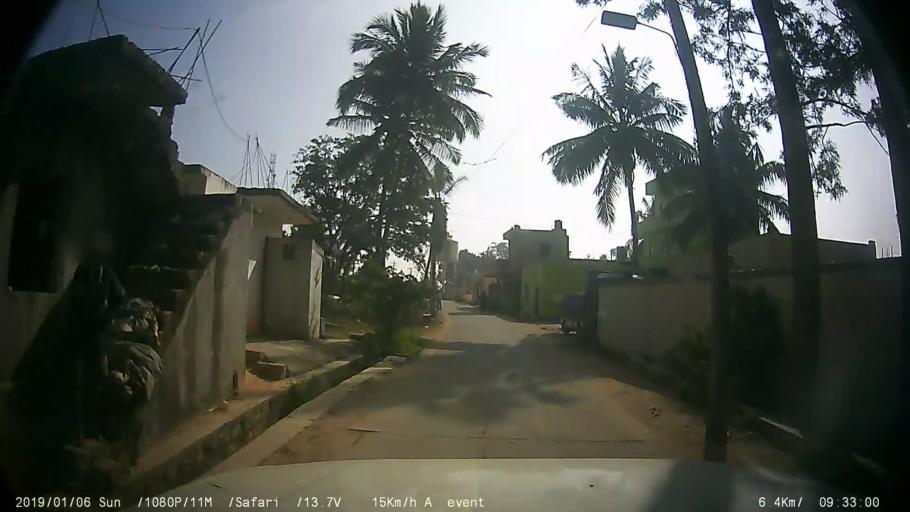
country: IN
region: Karnataka
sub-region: Bangalore Urban
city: Anekal
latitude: 12.8178
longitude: 77.6375
